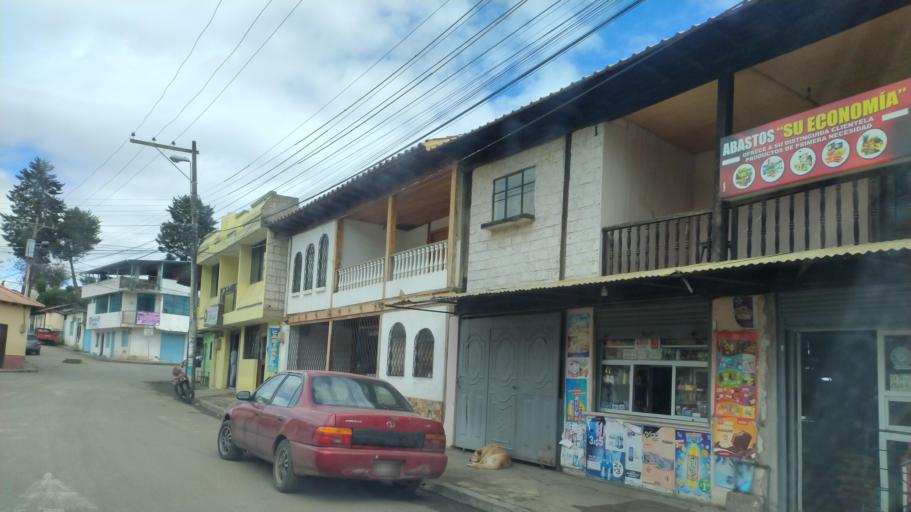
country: EC
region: Chimborazo
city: Riobamba
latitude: -1.6579
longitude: -78.5676
